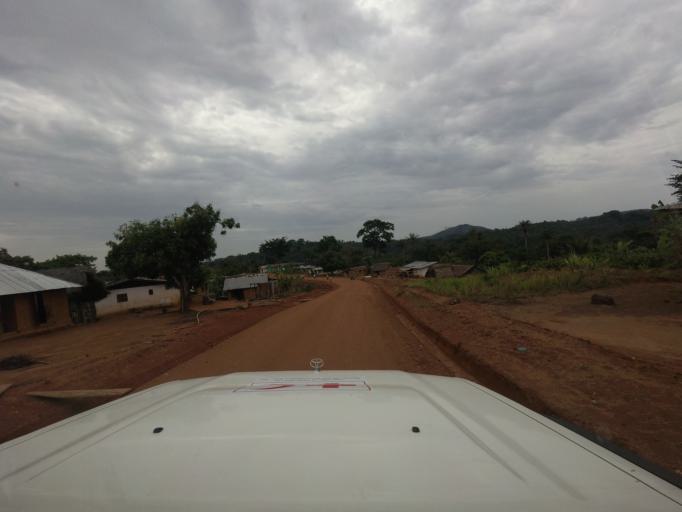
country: SL
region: Eastern Province
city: Buedu
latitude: 8.2145
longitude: -10.2259
